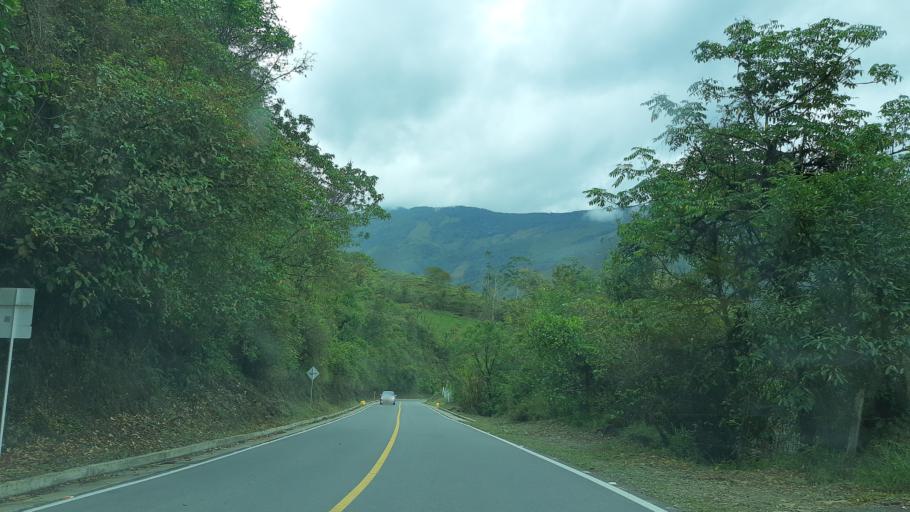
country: CO
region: Boyaca
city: Chivor
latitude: 4.9573
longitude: -73.3124
